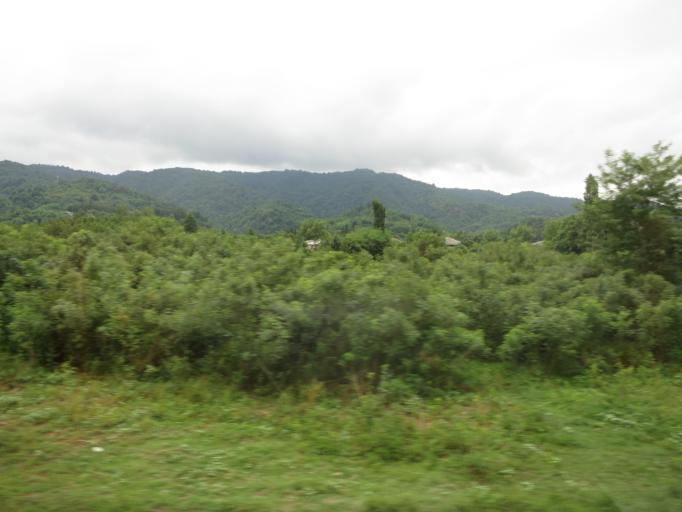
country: GE
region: Guria
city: Lanchkhuti
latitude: 42.0875
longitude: 42.1067
